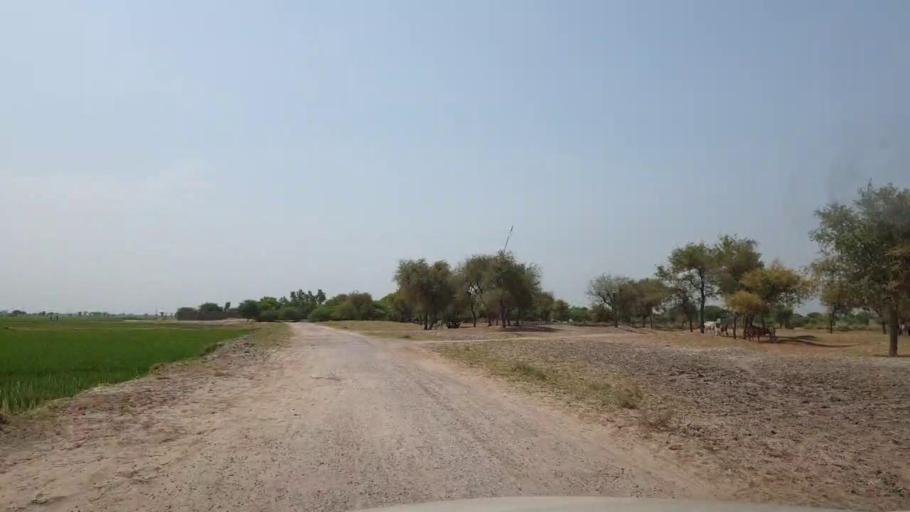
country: PK
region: Sindh
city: Ratodero
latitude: 27.8431
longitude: 68.2635
